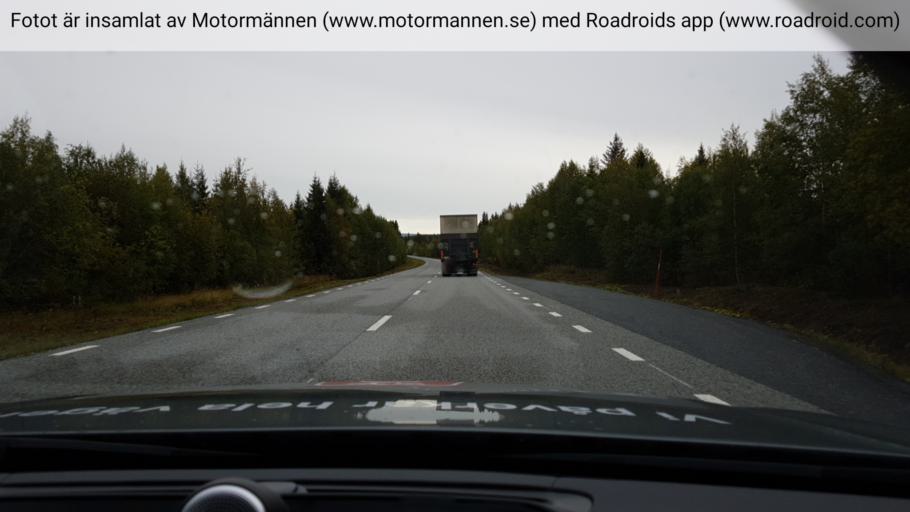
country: SE
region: Jaemtland
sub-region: Stroemsunds Kommun
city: Stroemsund
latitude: 64.1282
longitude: 15.6509
